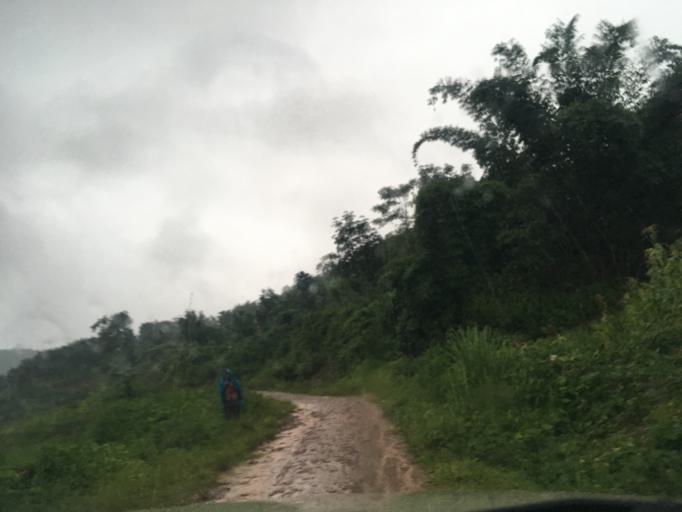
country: LA
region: Oudomxai
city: Muang La
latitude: 21.2415
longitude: 101.9502
